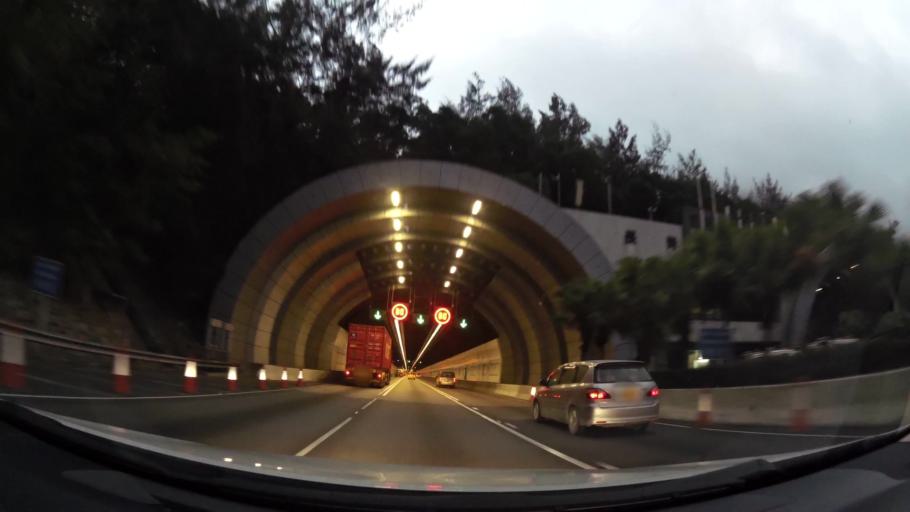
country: HK
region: Tsuen Wan
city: Tsuen Wan
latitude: 22.3450
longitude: 114.0957
